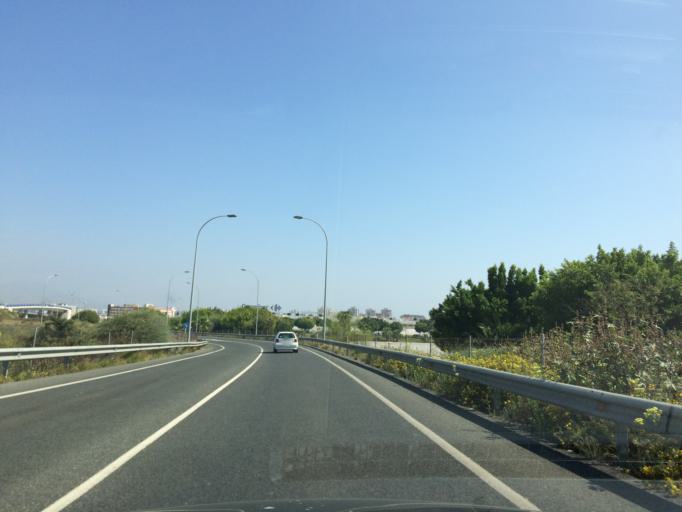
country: ES
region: Andalusia
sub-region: Provincia de Malaga
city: Malaga
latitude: 36.6832
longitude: -4.4615
